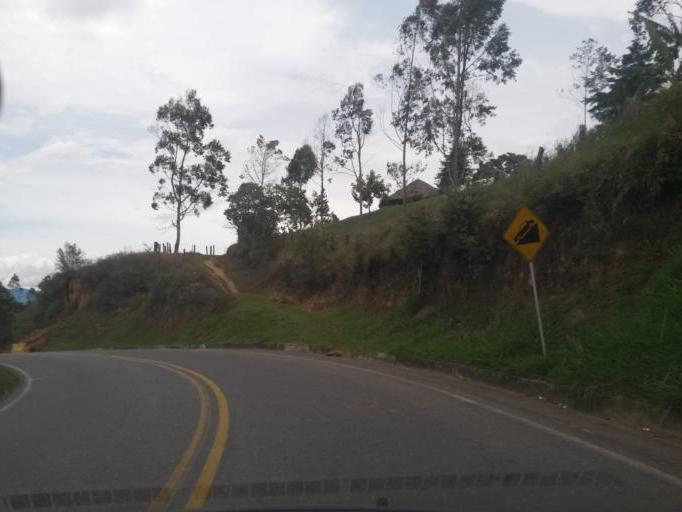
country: CO
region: Cauca
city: Lopez
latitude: 2.4340
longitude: -76.7572
